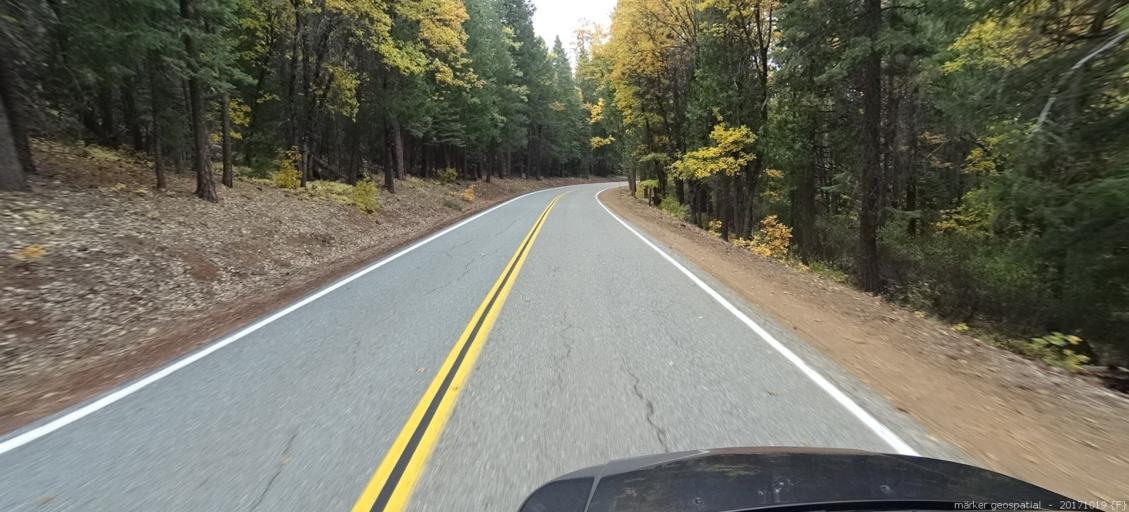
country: US
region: California
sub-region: Shasta County
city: Burney
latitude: 41.1195
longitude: -121.5899
